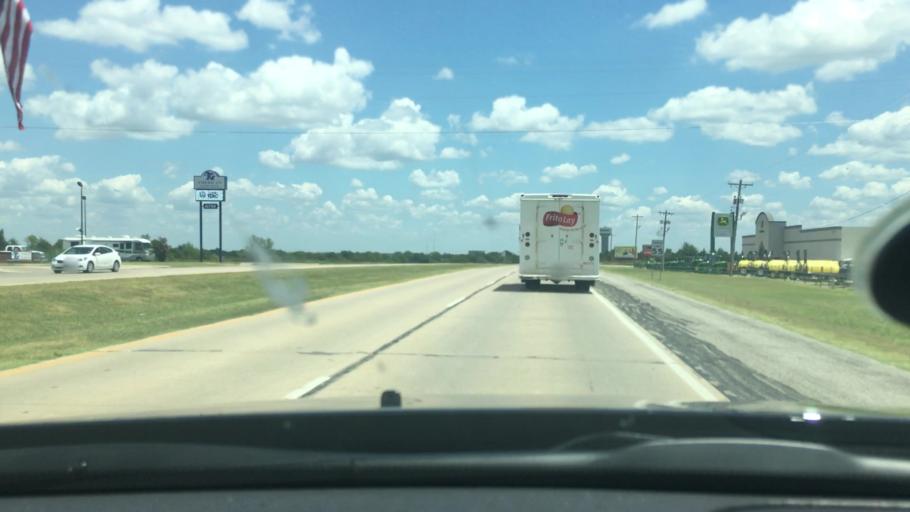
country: US
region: Oklahoma
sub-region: Carter County
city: Lone Grove
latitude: 34.1728
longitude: -97.2110
